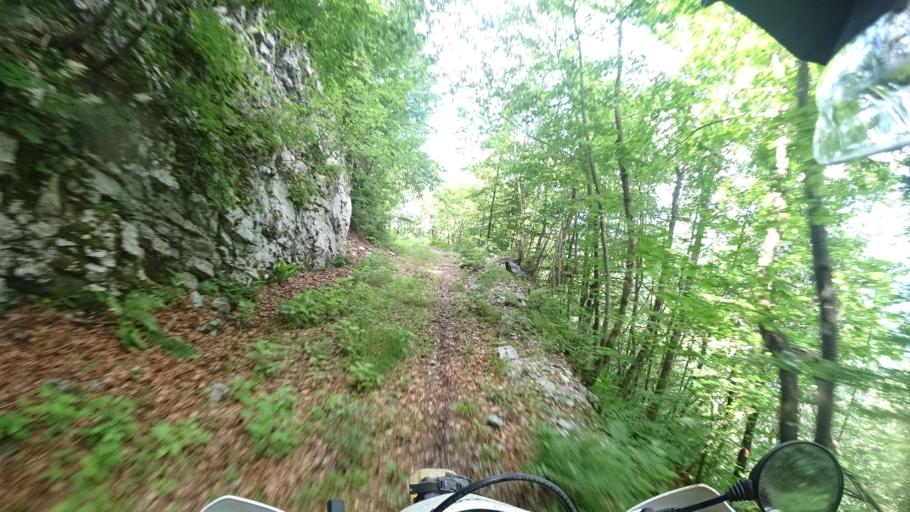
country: SI
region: Osilnica
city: Osilnica
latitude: 45.5018
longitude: 14.7117
